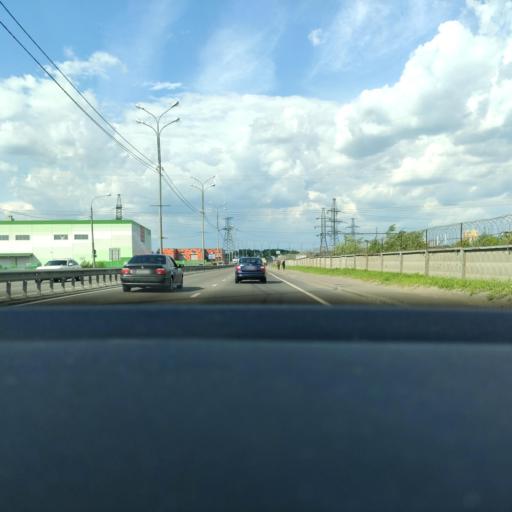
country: RU
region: Moscow
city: Vatutino
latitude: 55.9162
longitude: 37.6798
